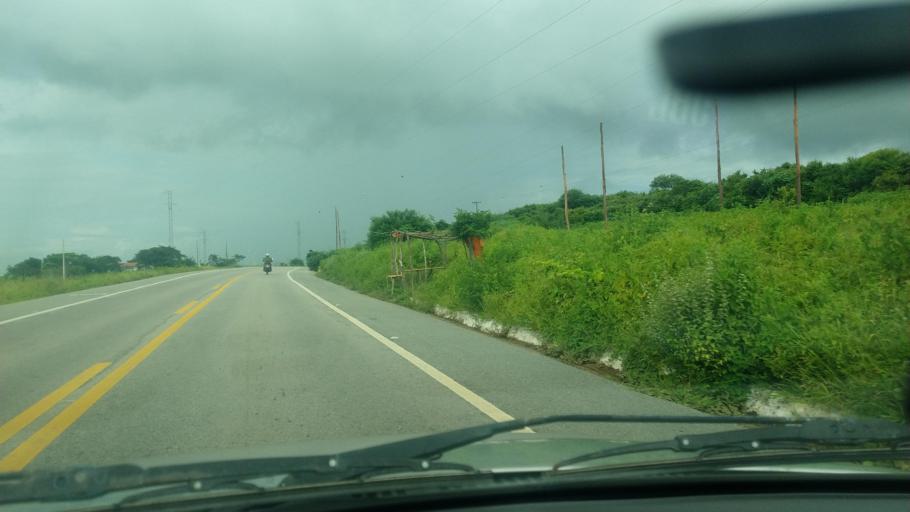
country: BR
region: Rio Grande do Norte
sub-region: Santa Cruz
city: Santa Cruz
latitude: -6.1940
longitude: -36.2080
